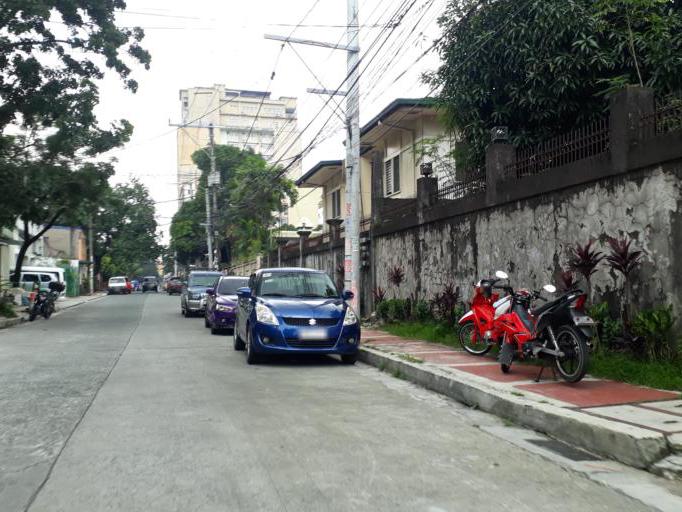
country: PH
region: Calabarzon
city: Bagong Pagasa
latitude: 14.6586
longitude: 121.0351
